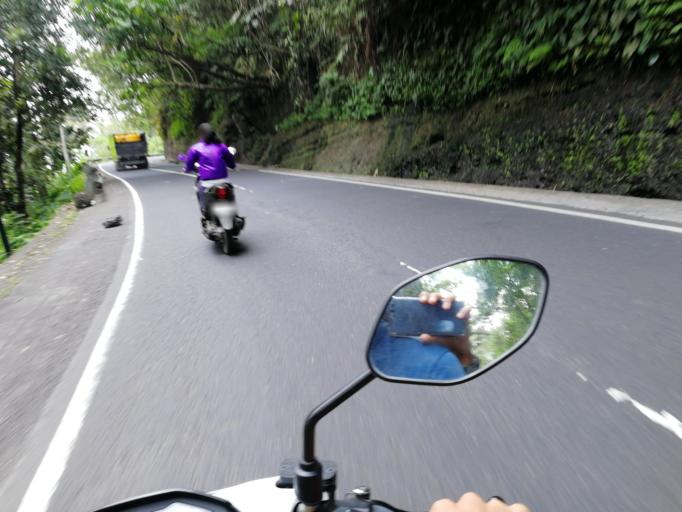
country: ID
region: Bali
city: Banjar Geriana Kangin
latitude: -8.4250
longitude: 115.4342
